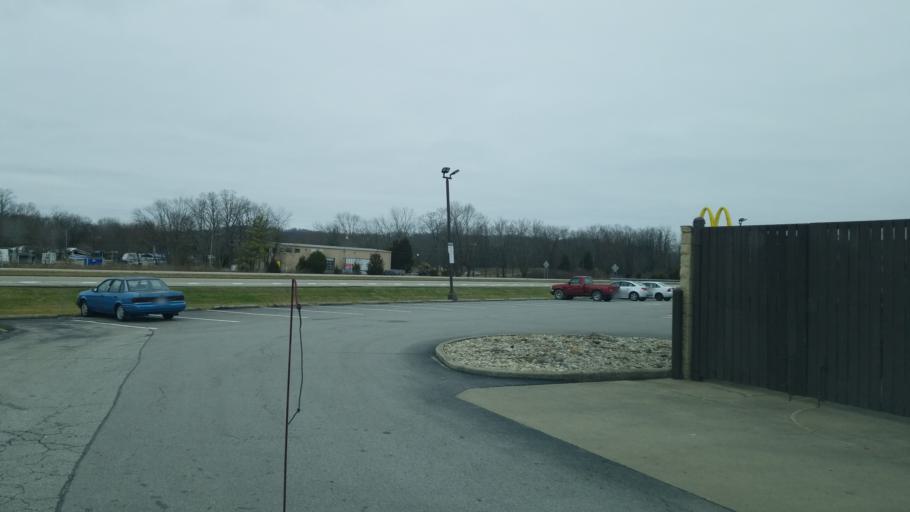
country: US
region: Ohio
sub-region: Clermont County
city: New Richmond
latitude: 38.9672
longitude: -84.2863
